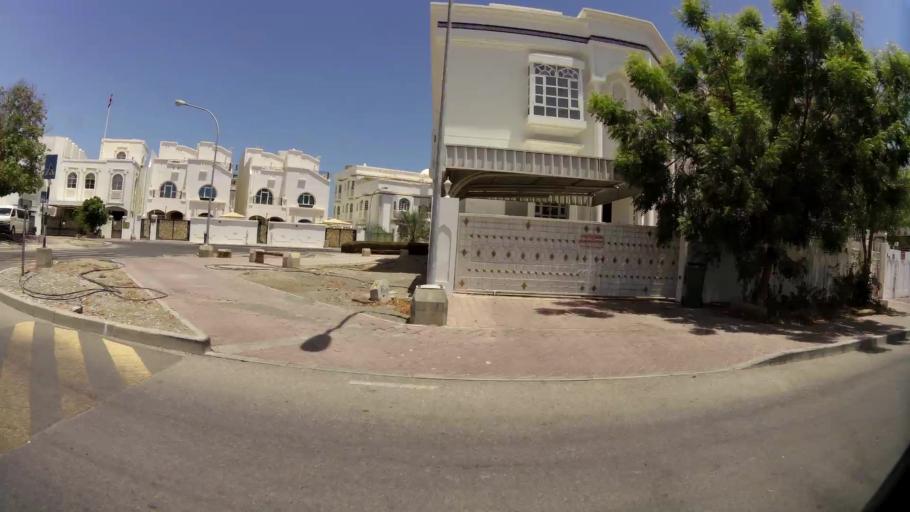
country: OM
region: Muhafazat Masqat
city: Bawshar
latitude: 23.6100
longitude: 58.4581
